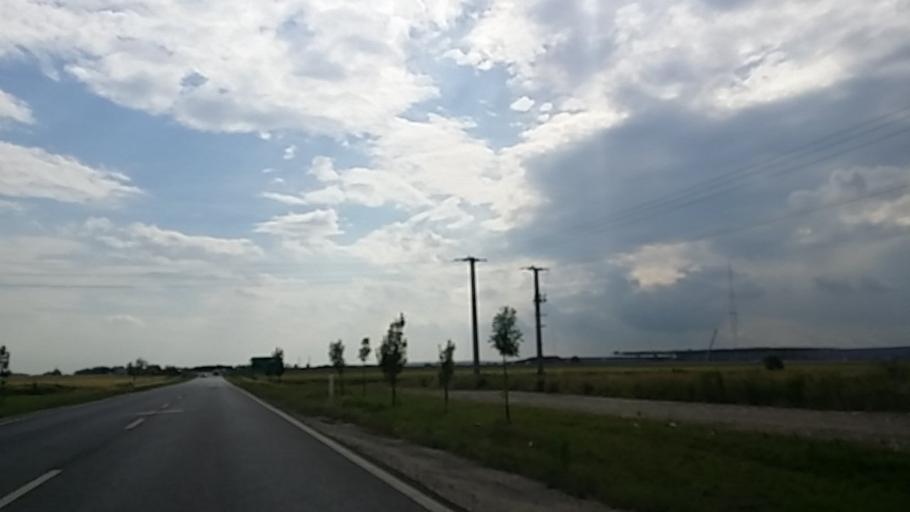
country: HU
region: Pest
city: Szigetszentmiklos
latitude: 47.3730
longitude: 19.0371
